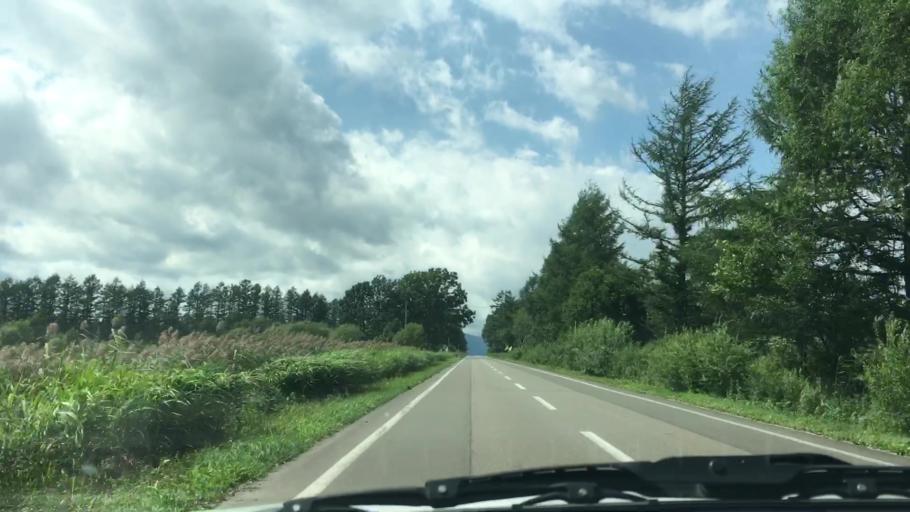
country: JP
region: Hokkaido
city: Otofuke
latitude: 43.2783
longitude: 143.3561
